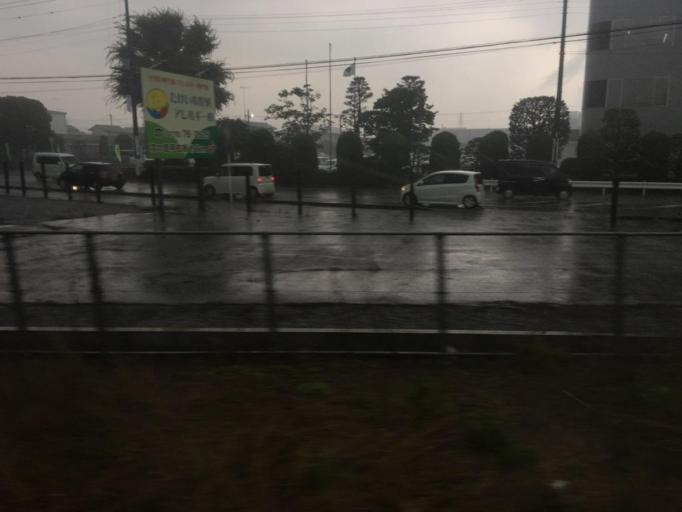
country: JP
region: Gunma
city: Tatebayashi
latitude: 36.2561
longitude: 139.5204
